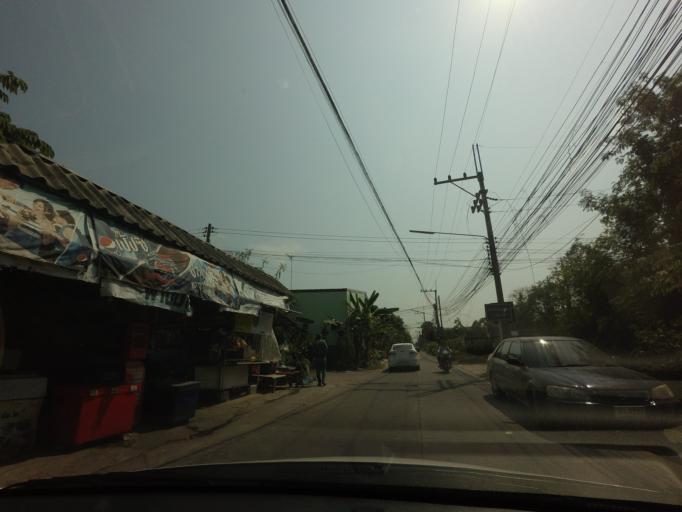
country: TH
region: Nakhon Pathom
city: Sam Phran
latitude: 13.7234
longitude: 100.2675
